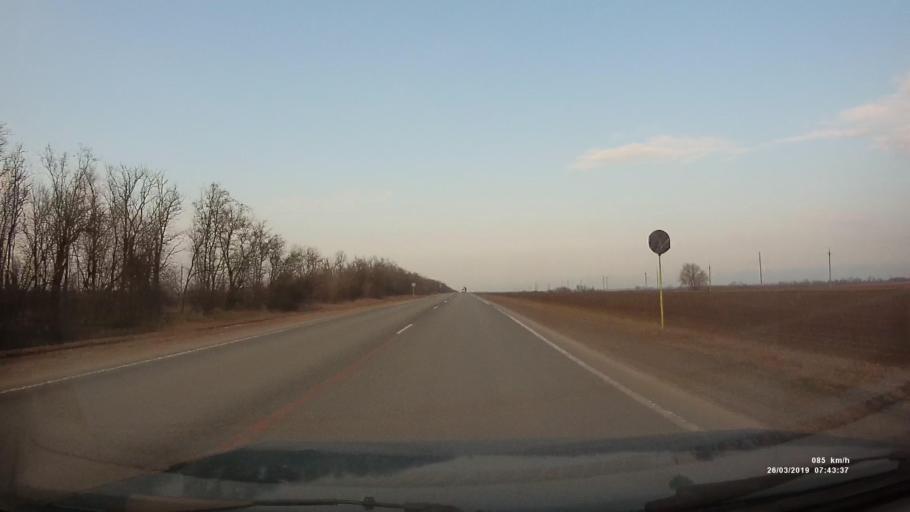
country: RU
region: Rostov
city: Novobessergenovka
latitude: 47.1816
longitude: 38.5917
